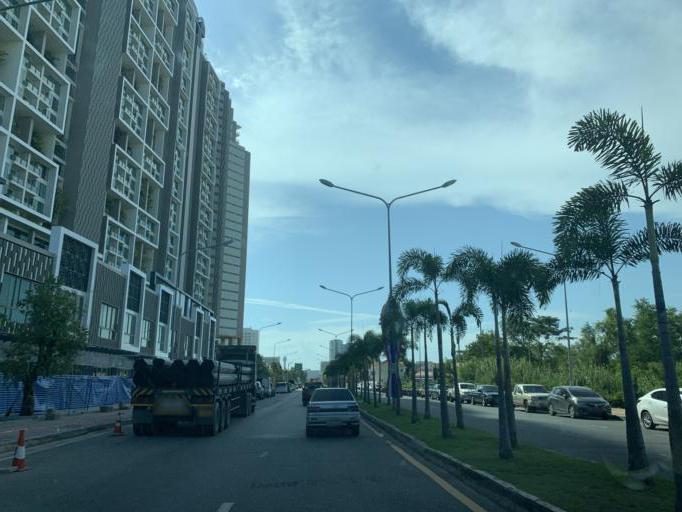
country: TH
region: Chon Buri
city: Phatthaya
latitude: 12.8824
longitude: 100.8866
